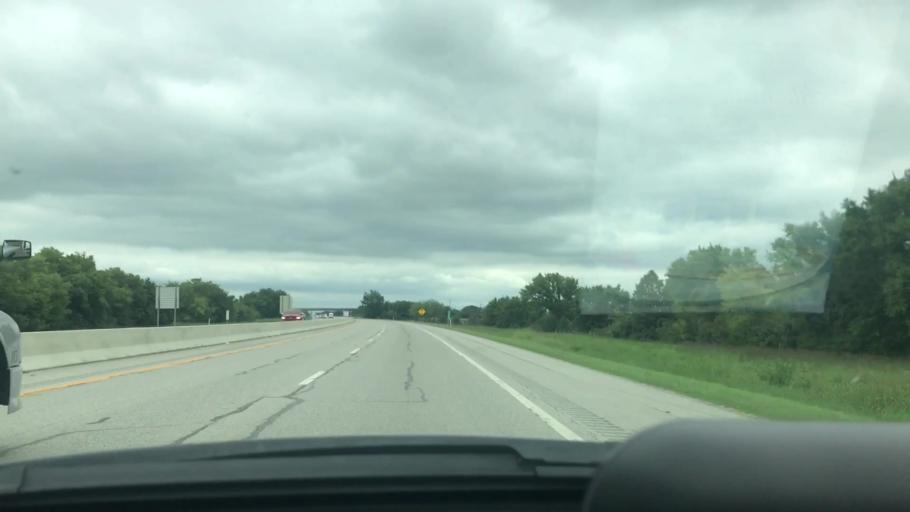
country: US
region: Oklahoma
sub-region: Ottawa County
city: Fairland
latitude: 36.7371
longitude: -94.9119
